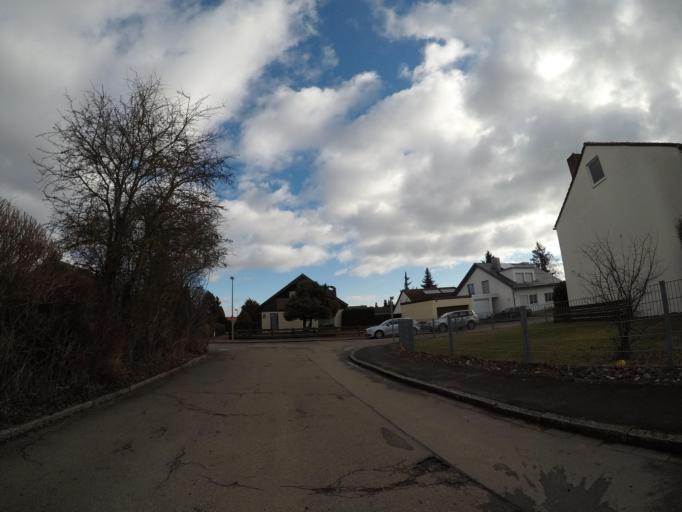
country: DE
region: Baden-Wuerttemberg
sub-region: Tuebingen Region
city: Dornstadt
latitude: 48.4352
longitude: 9.9659
